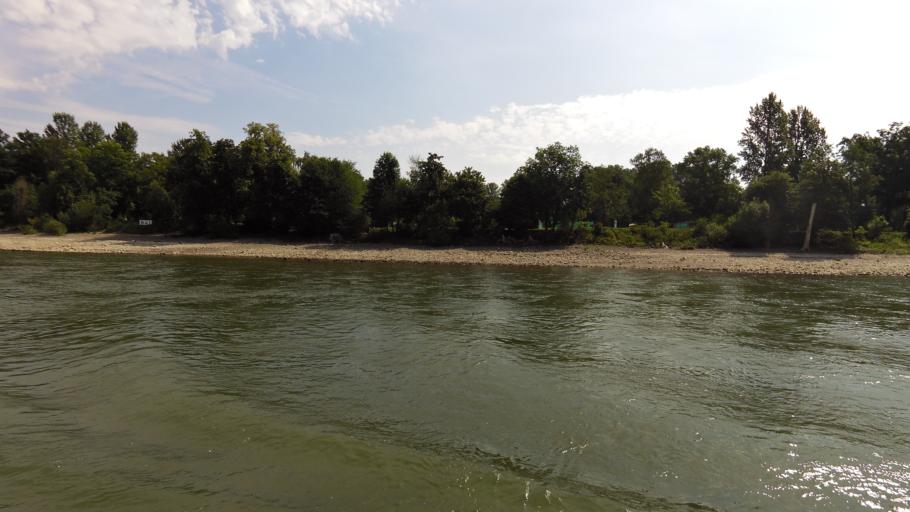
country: DE
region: North Rhine-Westphalia
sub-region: Regierungsbezirk Koln
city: Bad Honnef
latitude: 50.6384
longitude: 7.2124
